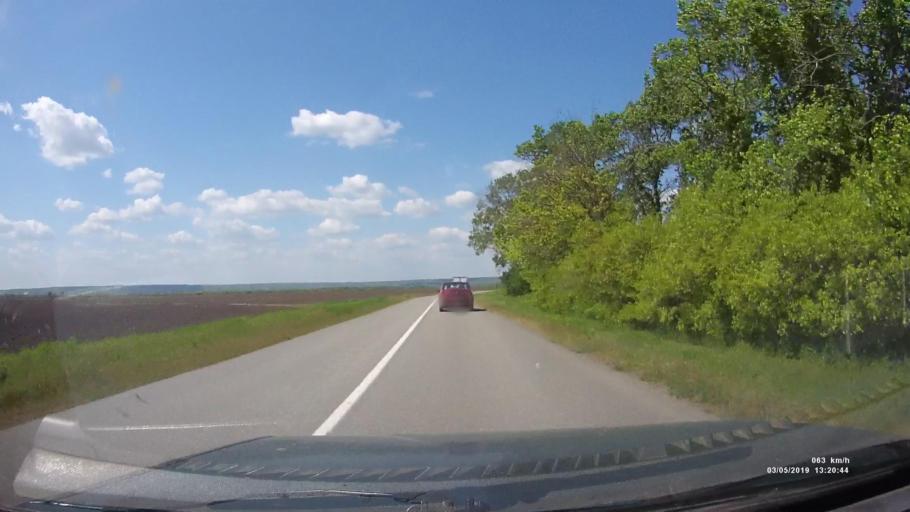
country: RU
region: Rostov
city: Semikarakorsk
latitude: 47.5487
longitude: 40.7513
